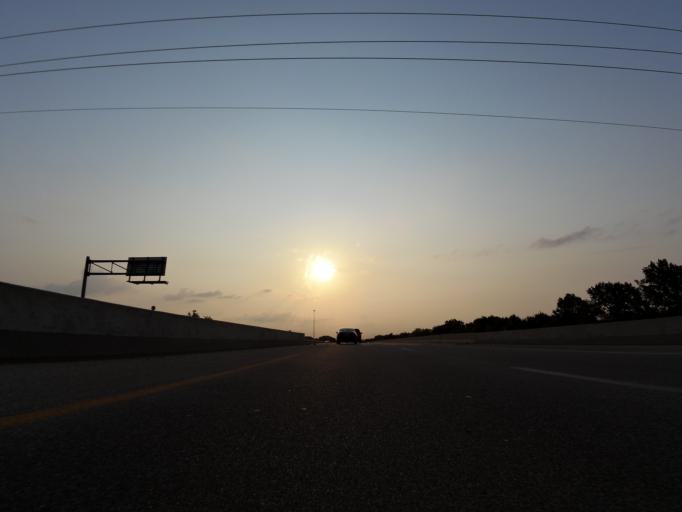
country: US
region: Kansas
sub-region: Sedgwick County
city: Bellaire
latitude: 37.7455
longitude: -97.2807
